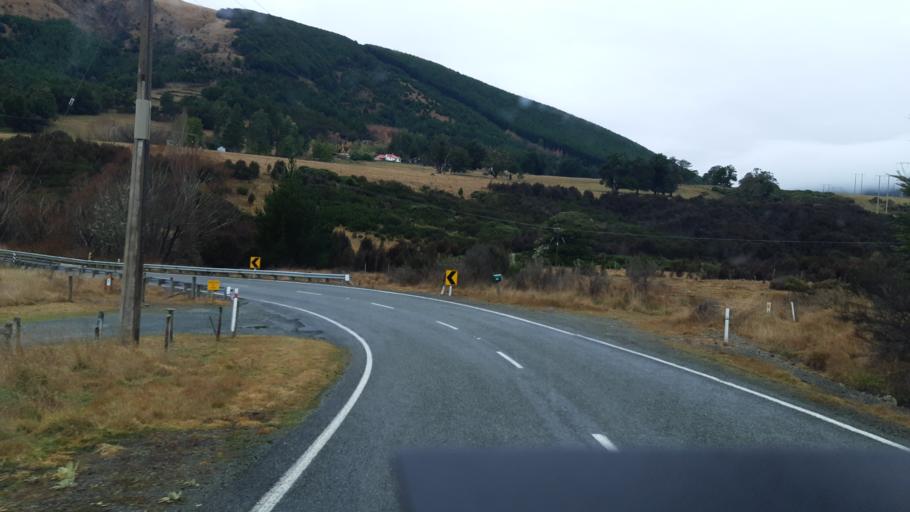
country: NZ
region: Tasman
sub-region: Tasman District
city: Wakefield
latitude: -41.7637
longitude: 172.8949
